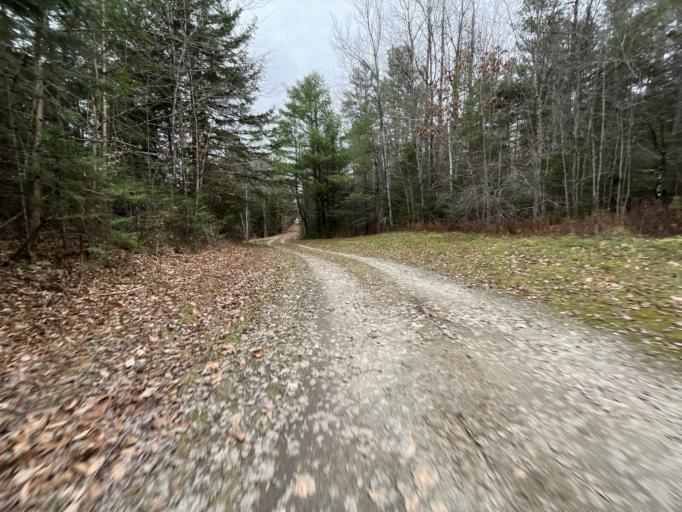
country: US
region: New Hampshire
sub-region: Merrimack County
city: New London
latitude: 43.4055
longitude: -71.9823
